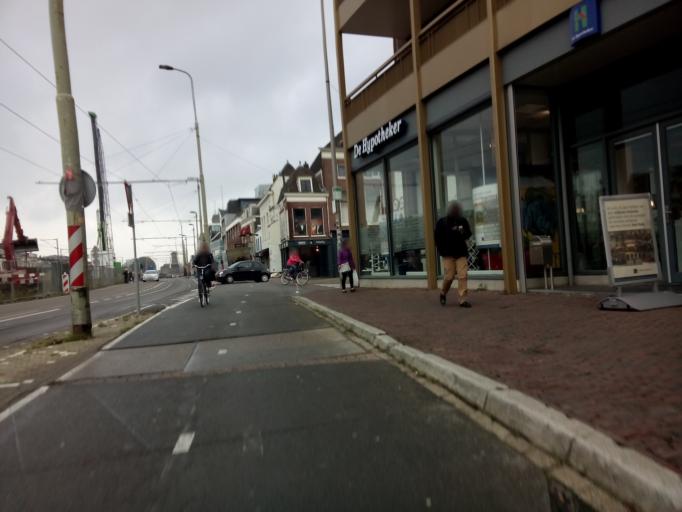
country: NL
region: South Holland
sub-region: Gemeente Delft
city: Delft
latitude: 52.0092
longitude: 4.3561
